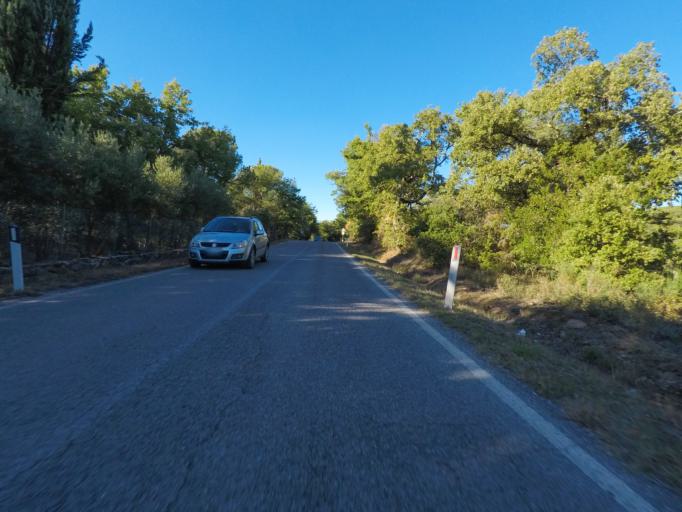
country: IT
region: Tuscany
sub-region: Provincia di Siena
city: Belverde
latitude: 43.4053
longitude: 11.3524
